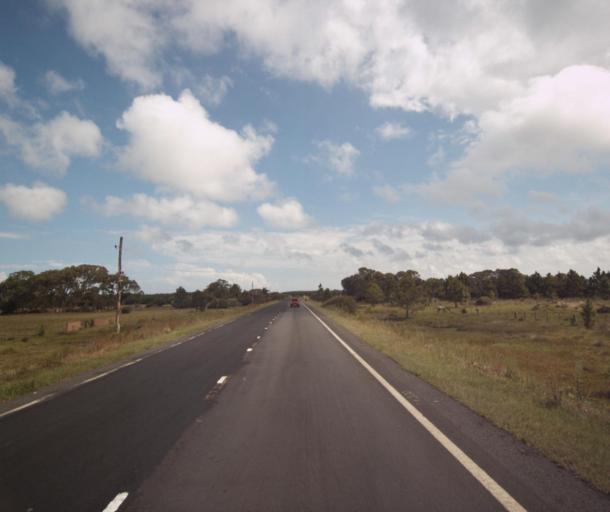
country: BR
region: Rio Grande do Sul
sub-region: Tapes
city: Tapes
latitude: -31.4076
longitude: -51.1673
